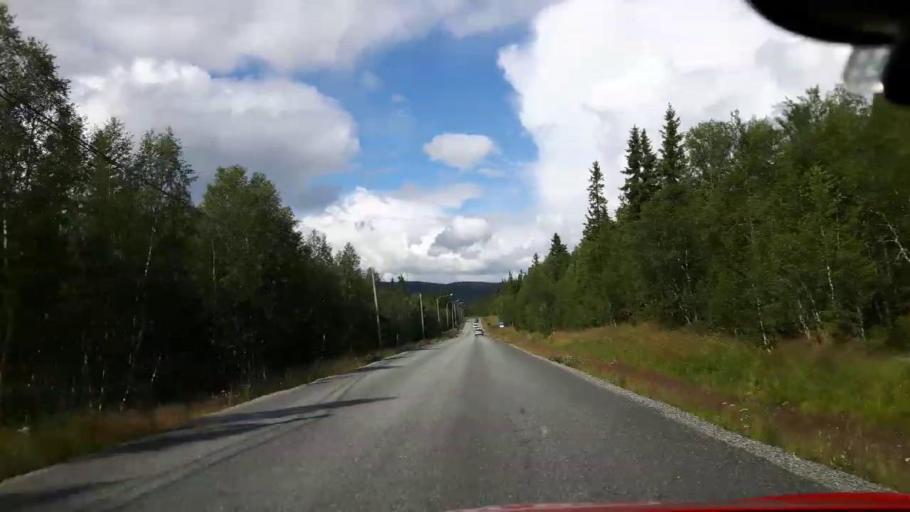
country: NO
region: Nordland
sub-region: Hattfjelldal
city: Hattfjelldal
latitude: 65.0621
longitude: 14.8812
